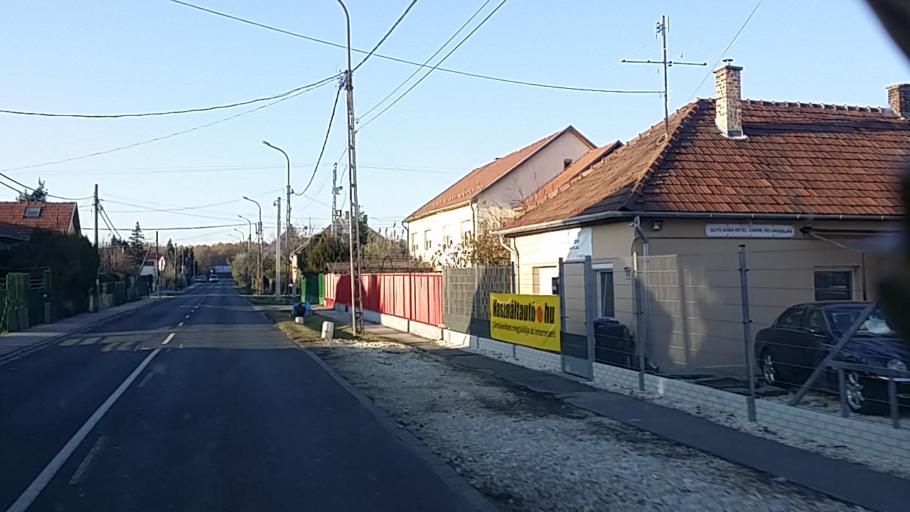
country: HU
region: Budapest
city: Budapest XVI. keruelet
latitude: 47.5359
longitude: 19.1667
